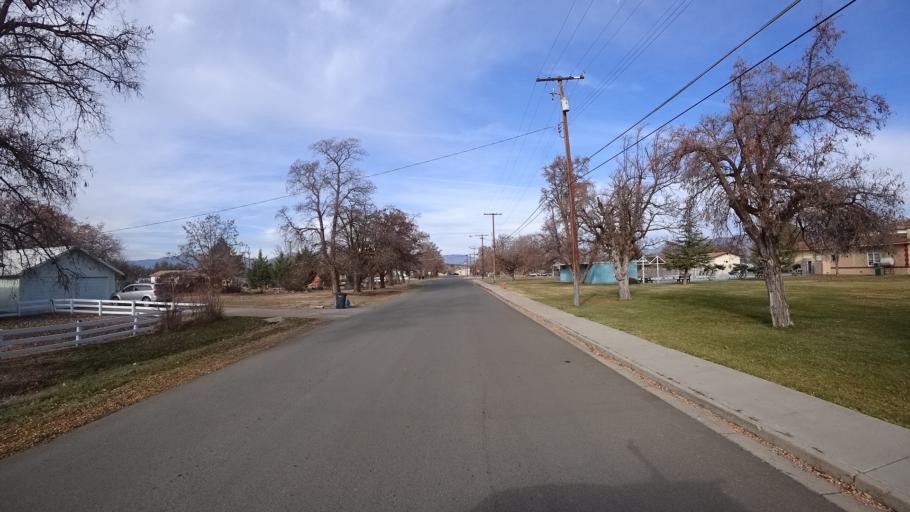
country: US
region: California
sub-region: Siskiyou County
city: Montague
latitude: 41.7270
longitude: -122.5320
